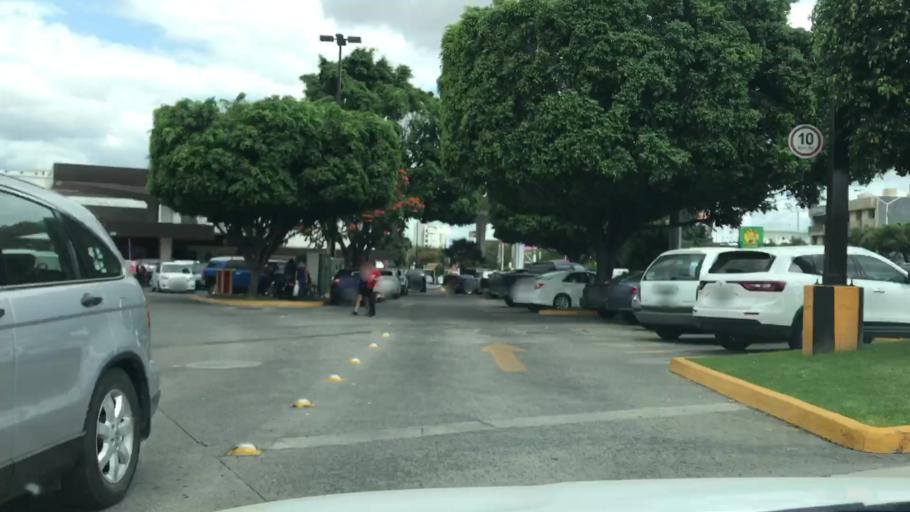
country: MX
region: Jalisco
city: Guadalajara
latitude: 20.6494
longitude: -103.4018
